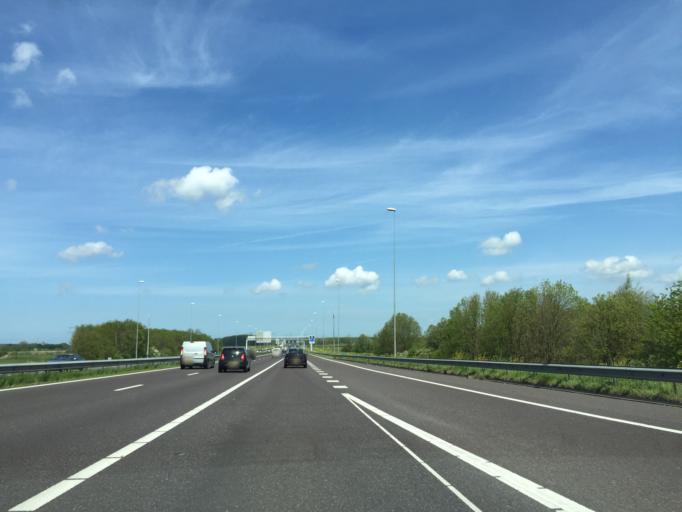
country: NL
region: North Holland
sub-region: Gemeente Haarlem
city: Haarlem
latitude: 52.3890
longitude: 4.7069
